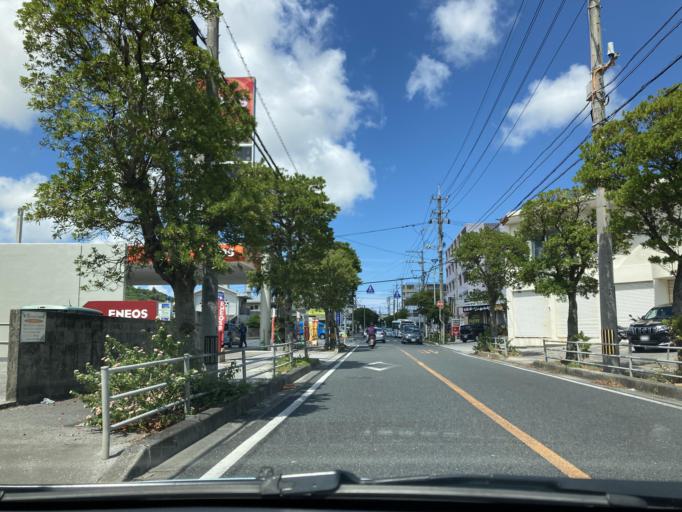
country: JP
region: Okinawa
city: Tomigusuku
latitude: 26.1830
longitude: 127.7137
